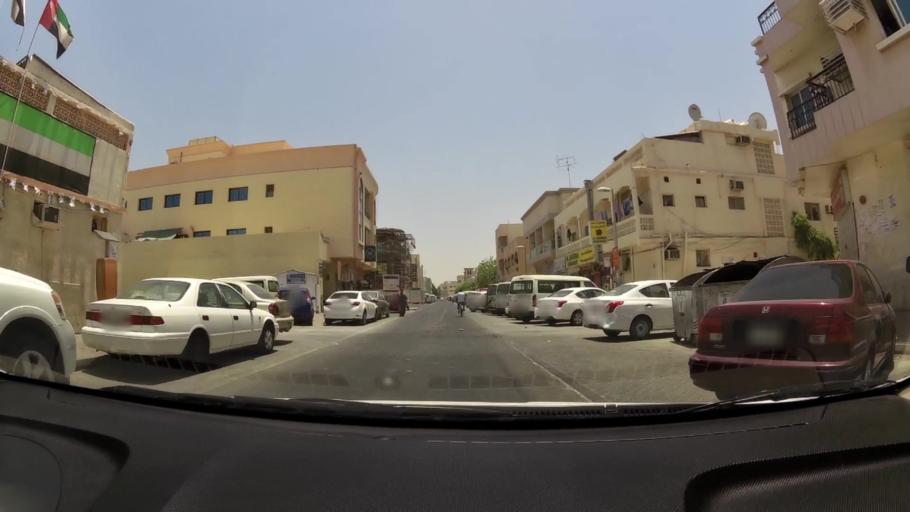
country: AE
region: Ash Shariqah
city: Sharjah
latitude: 25.2751
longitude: 55.3332
